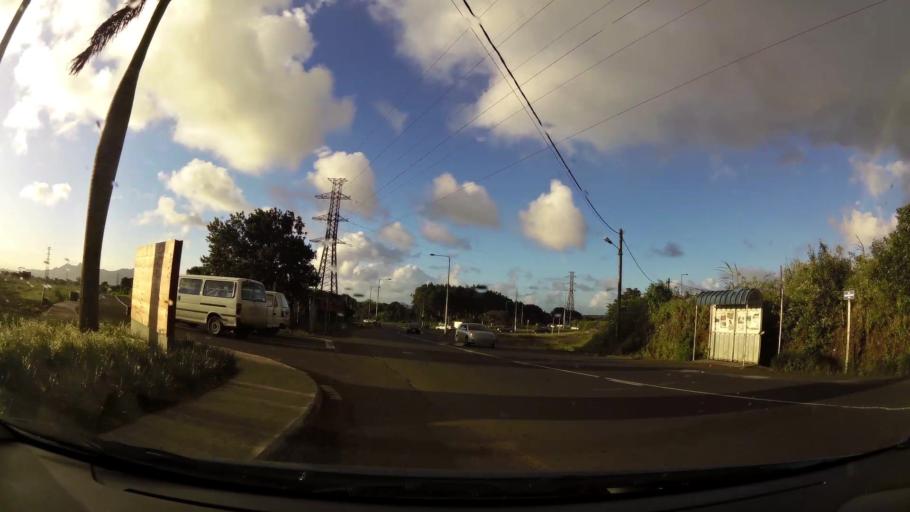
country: MU
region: Plaines Wilhems
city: Curepipe
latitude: -20.3003
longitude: 57.5354
